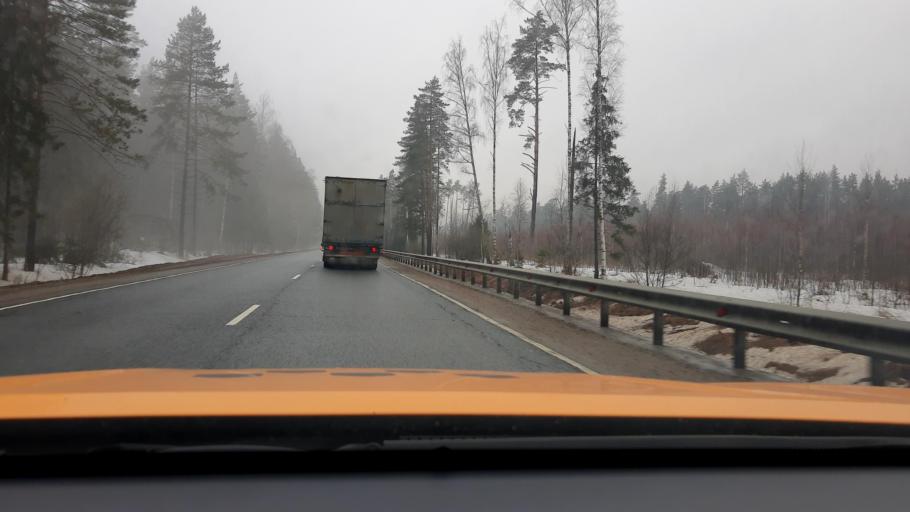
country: RU
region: Moskovskaya
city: Chernogolovka
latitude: 56.0178
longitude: 38.2487
